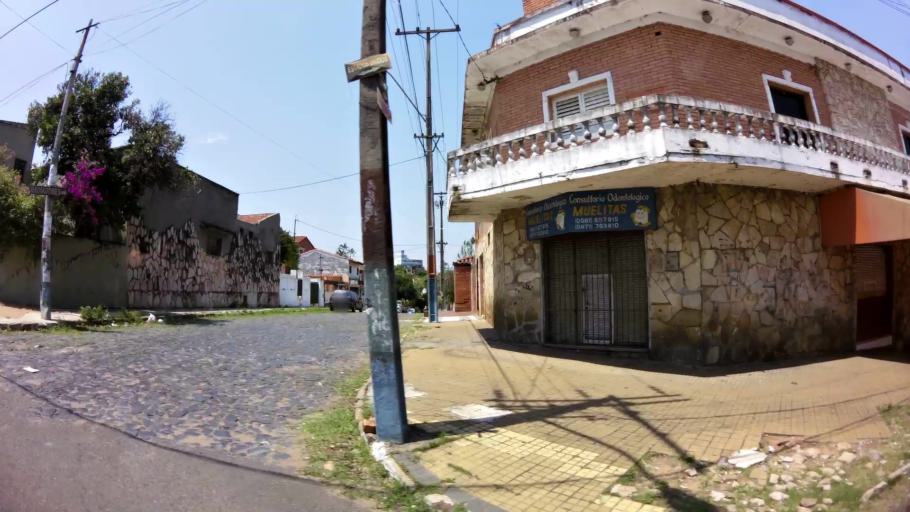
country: PY
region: Asuncion
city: Asuncion
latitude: -25.3011
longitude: -57.6358
